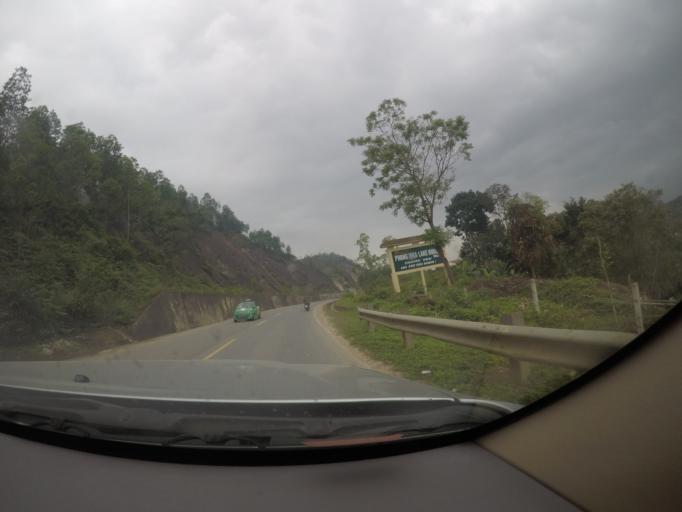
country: VN
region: Quang Binh
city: Ba Don
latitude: 17.6184
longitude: 106.3766
